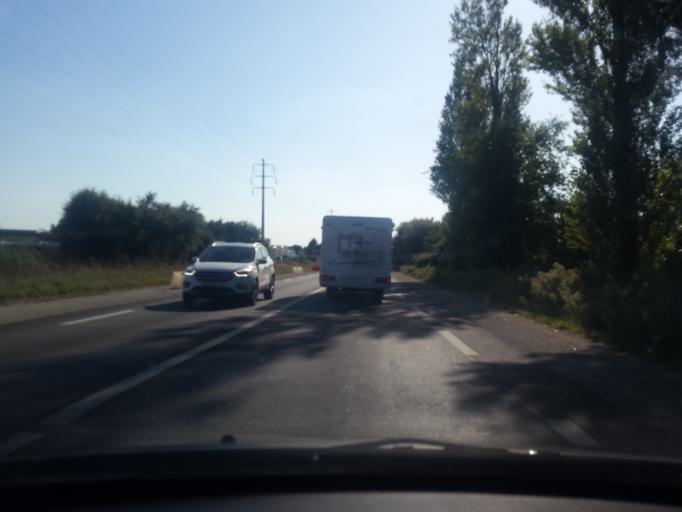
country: FR
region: Brittany
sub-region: Departement du Morbihan
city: Saint-Ave
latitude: 47.6820
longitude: -2.7683
